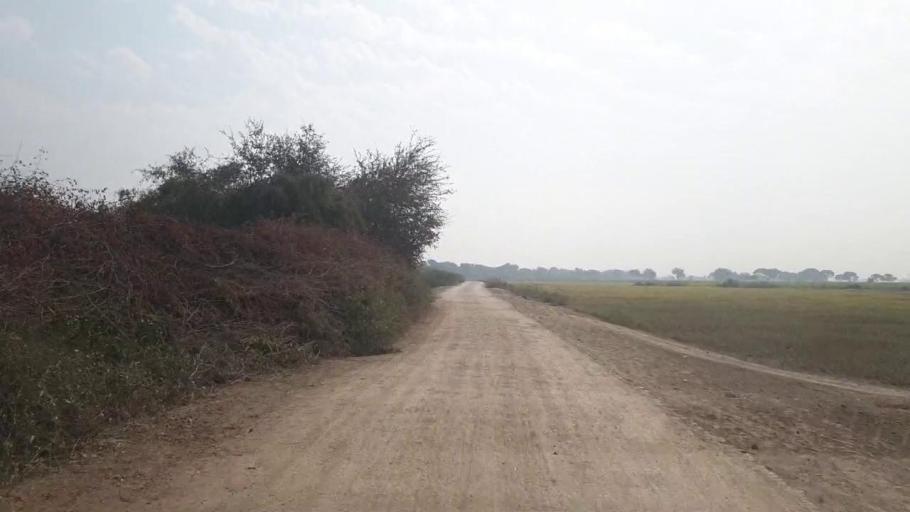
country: PK
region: Sindh
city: Hala
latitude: 25.7832
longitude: 68.4346
